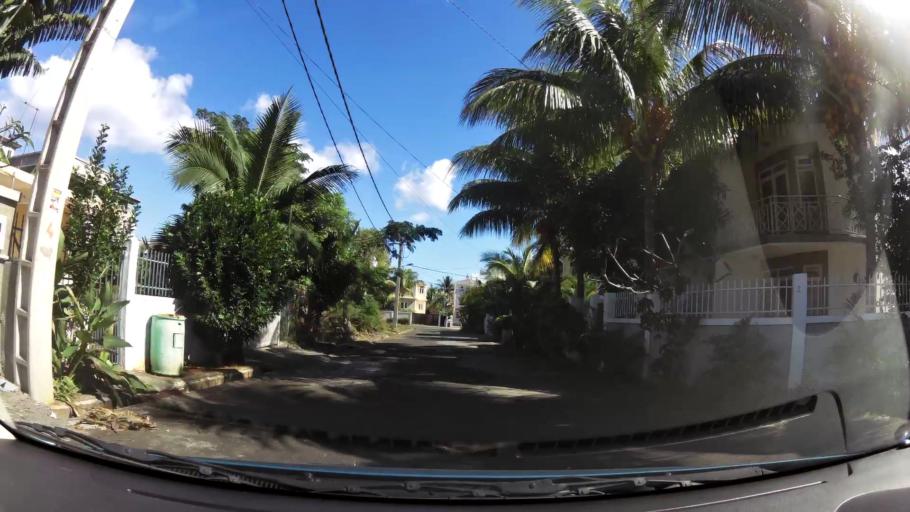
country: MU
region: Black River
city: Flic en Flac
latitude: -20.2850
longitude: 57.3717
